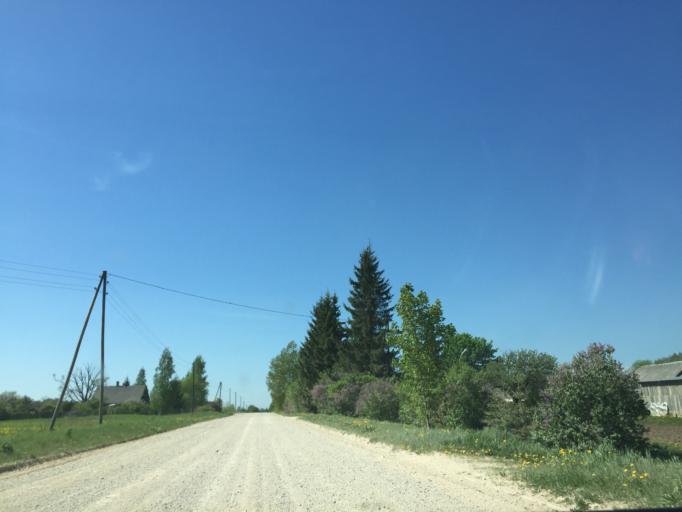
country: LV
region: Kegums
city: Kegums
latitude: 56.8646
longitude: 24.7663
